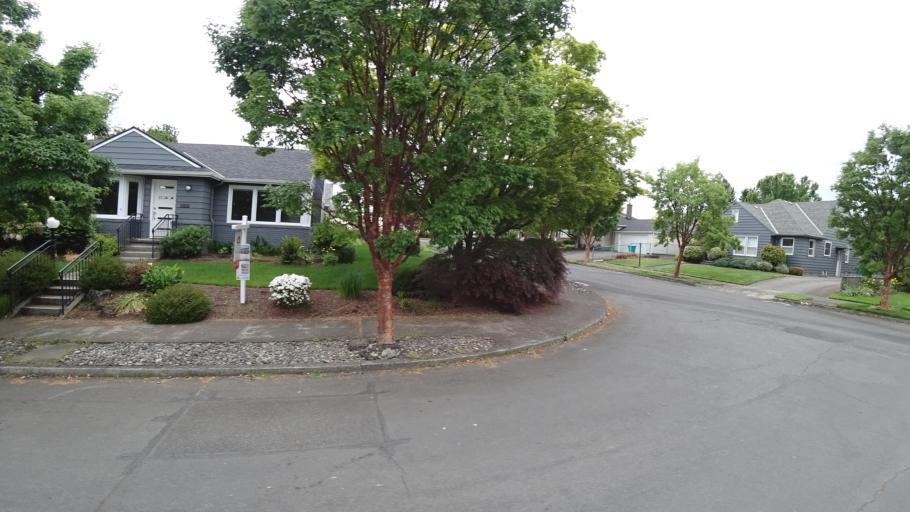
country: US
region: Oregon
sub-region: Multnomah County
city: Portland
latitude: 45.5219
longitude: -122.6142
